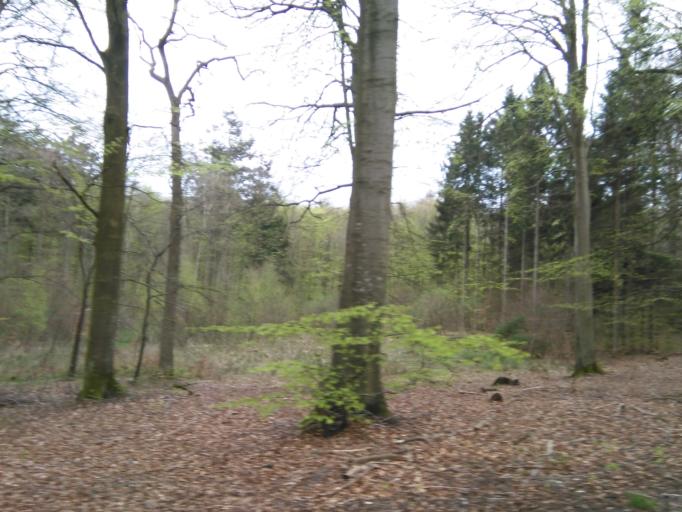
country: DK
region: Central Jutland
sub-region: Arhus Kommune
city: Beder
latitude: 56.0724
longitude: 10.2465
